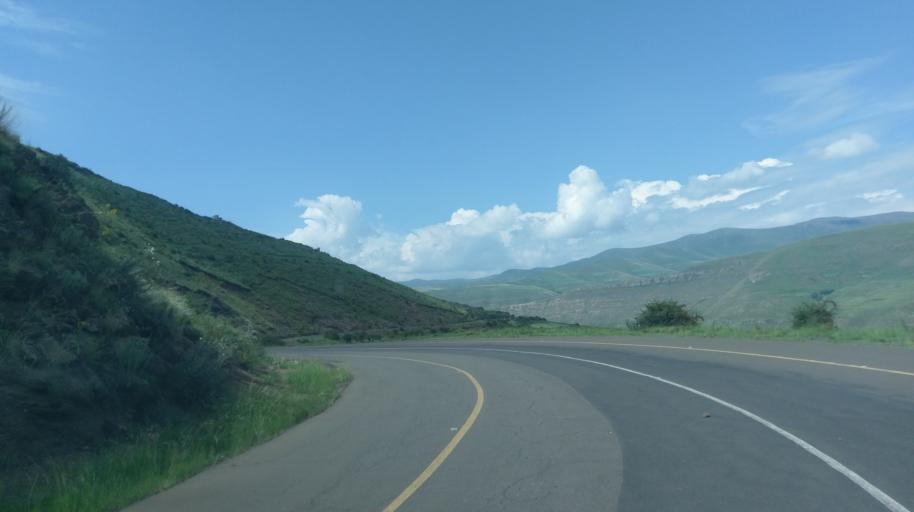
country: LS
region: Thaba-Tseka
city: Thaba-Tseka
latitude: -29.1510
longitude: 28.4839
